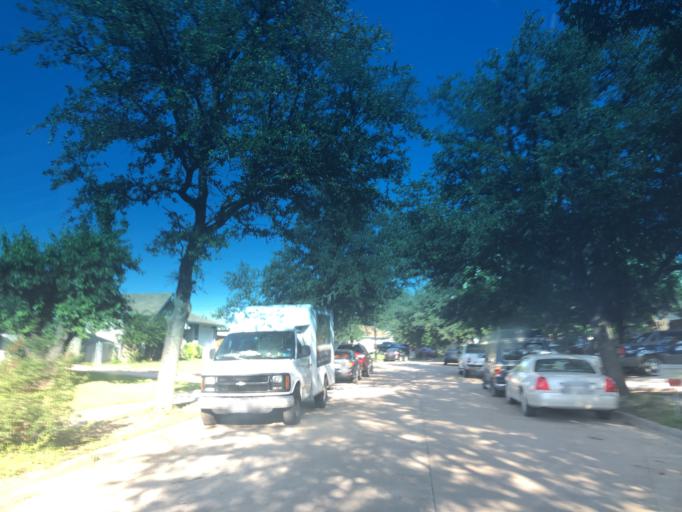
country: US
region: Texas
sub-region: Dallas County
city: Grand Prairie
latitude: 32.6942
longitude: -97.0000
